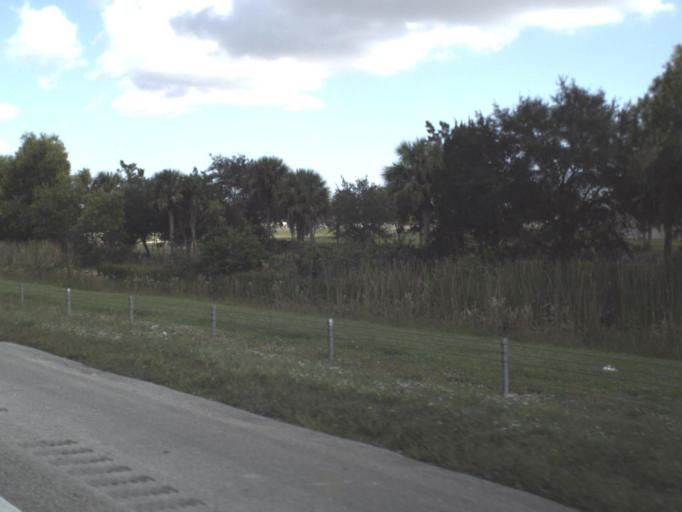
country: US
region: Florida
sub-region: Palm Beach County
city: Schall Circle
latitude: 26.7400
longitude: -80.1348
